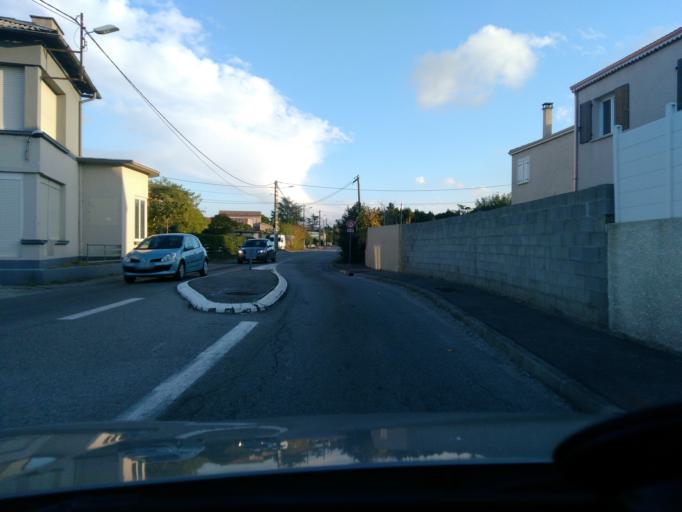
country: FR
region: Rhone-Alpes
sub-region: Departement de la Drome
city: Montelimar
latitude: 44.5352
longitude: 4.7396
